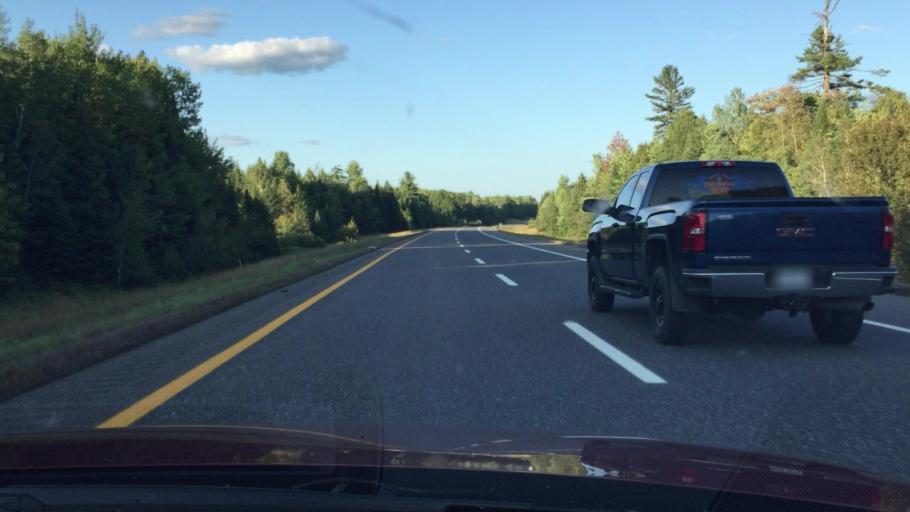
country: US
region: Maine
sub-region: Penobscot County
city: Patten
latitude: 46.0429
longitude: -68.2597
